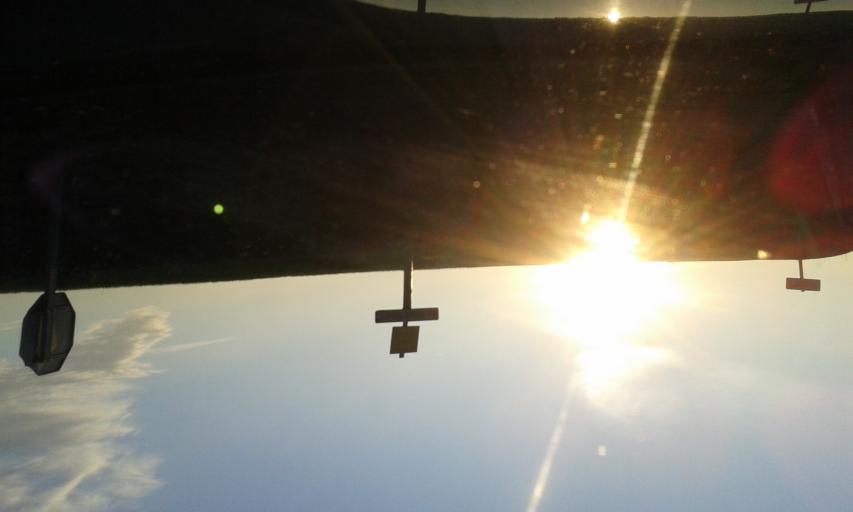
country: FR
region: Centre
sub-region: Departement du Loiret
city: Tavers
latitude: 47.7625
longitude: 1.6009
